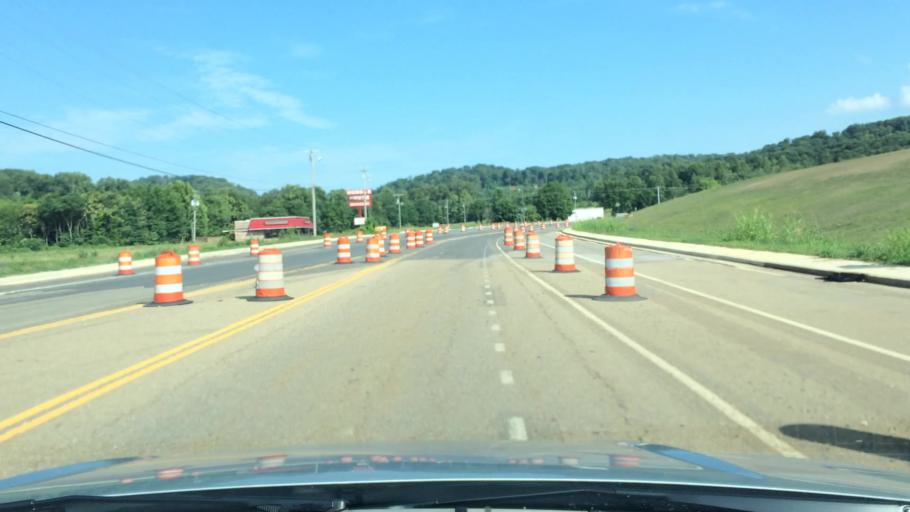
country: US
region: Tennessee
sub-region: Jefferson County
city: White Pine
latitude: 36.1106
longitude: -83.3399
